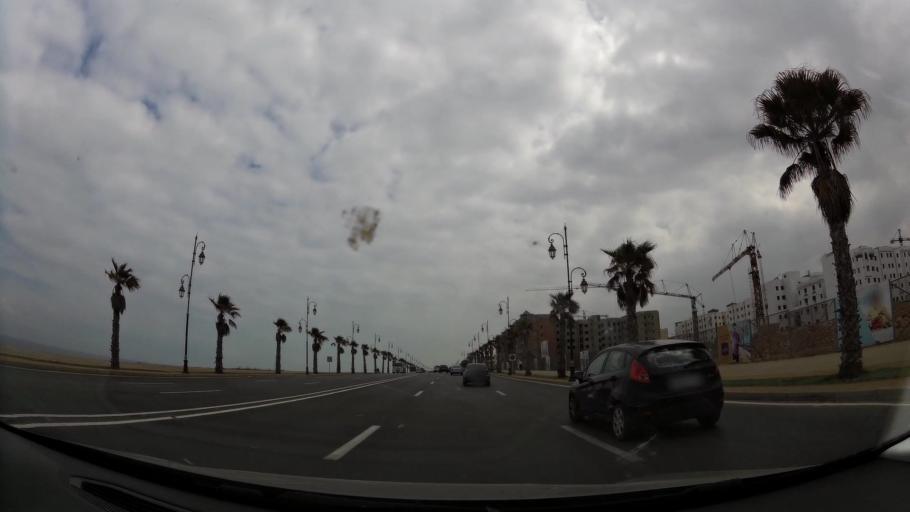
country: MA
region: Rabat-Sale-Zemmour-Zaer
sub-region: Rabat
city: Rabat
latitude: 33.9993
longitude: -6.8761
